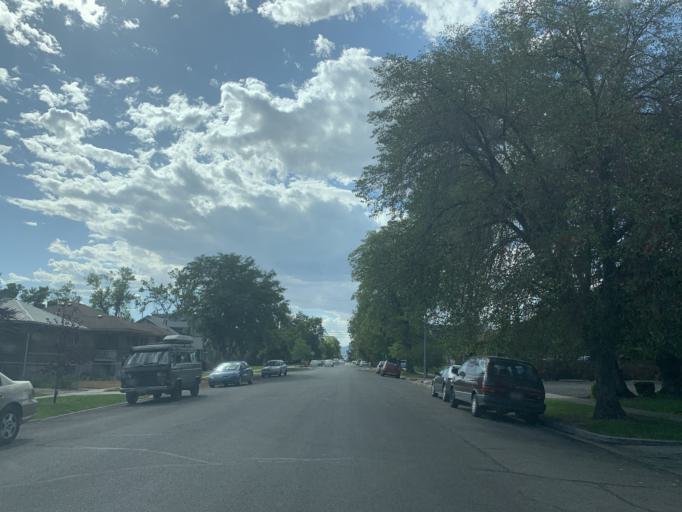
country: US
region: Utah
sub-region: Utah County
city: Provo
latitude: 40.2391
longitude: -111.6540
